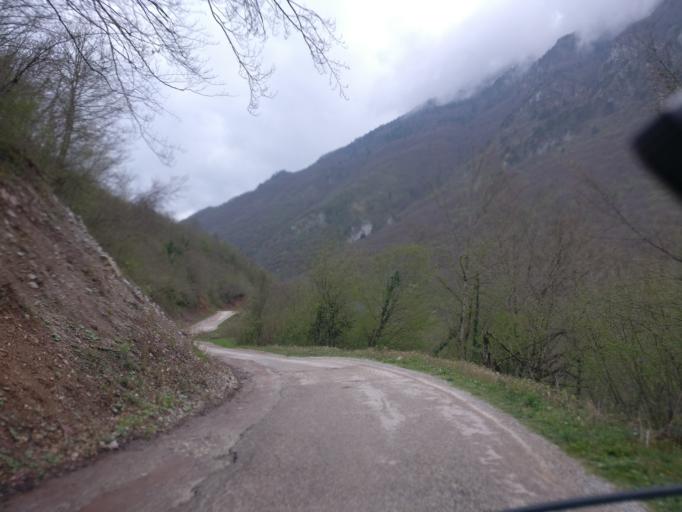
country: BA
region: Republika Srpska
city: Foca
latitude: 43.3580
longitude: 18.8156
